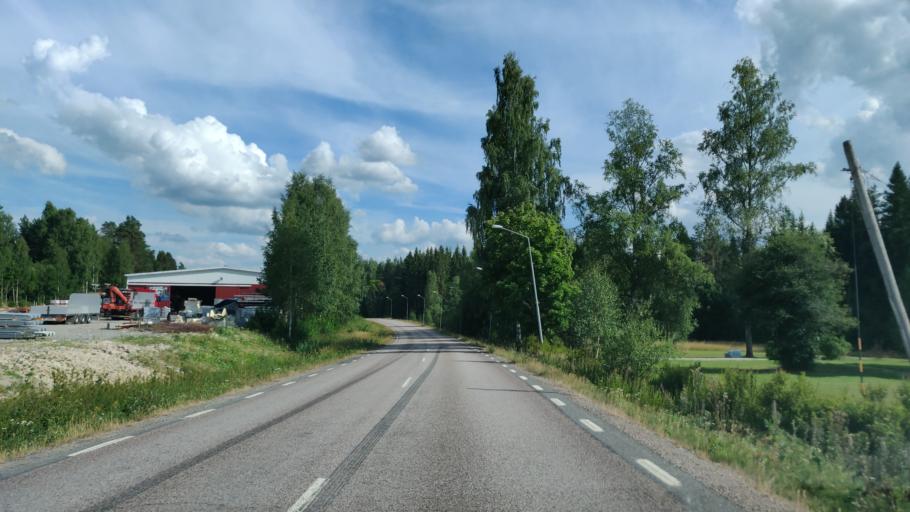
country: SE
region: Vaermland
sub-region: Hagfors Kommun
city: Hagfors
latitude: 60.0699
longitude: 13.6329
